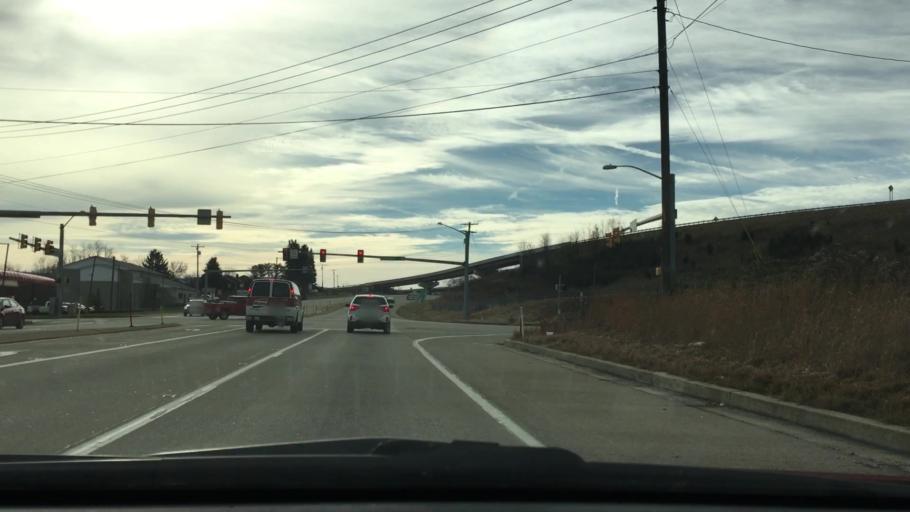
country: US
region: Pennsylvania
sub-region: Fayette County
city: Oliver
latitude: 39.9228
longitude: -79.7267
